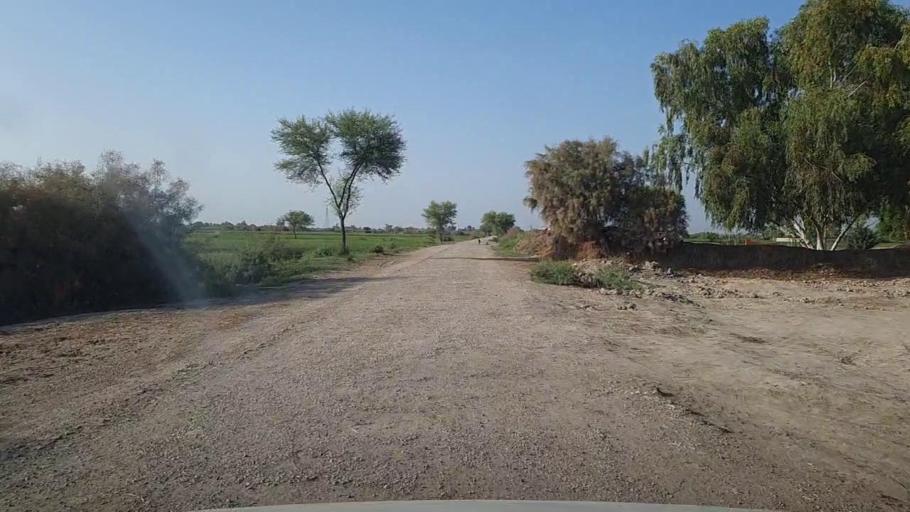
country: PK
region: Sindh
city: Kandhkot
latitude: 28.3005
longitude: 69.3288
